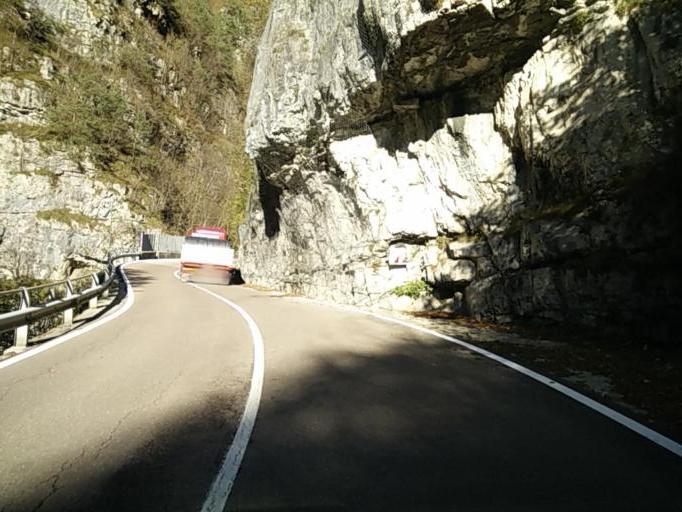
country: IT
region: Trentino-Alto Adige
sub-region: Provincia di Trento
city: Storo
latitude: 45.8476
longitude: 10.6264
